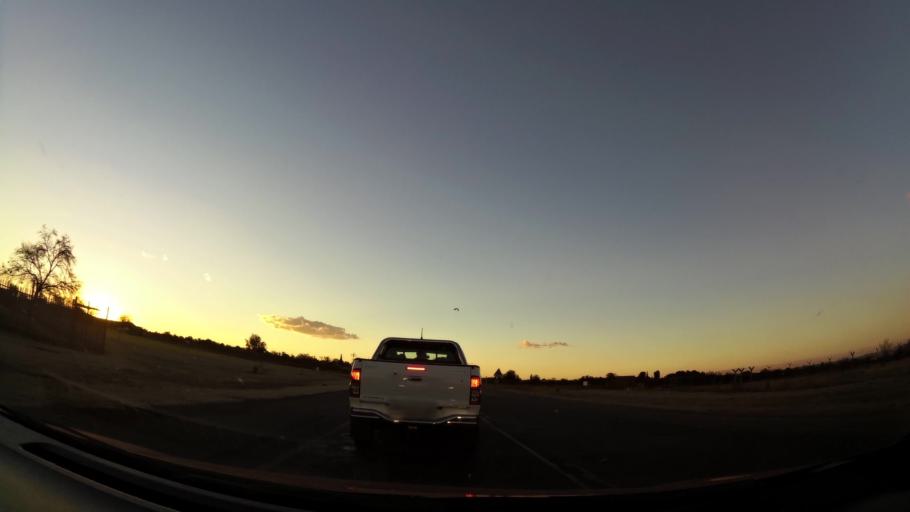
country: ZA
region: North-West
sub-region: Dr Kenneth Kaunda District Municipality
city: Potchefstroom
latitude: -26.6782
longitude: 27.0742
